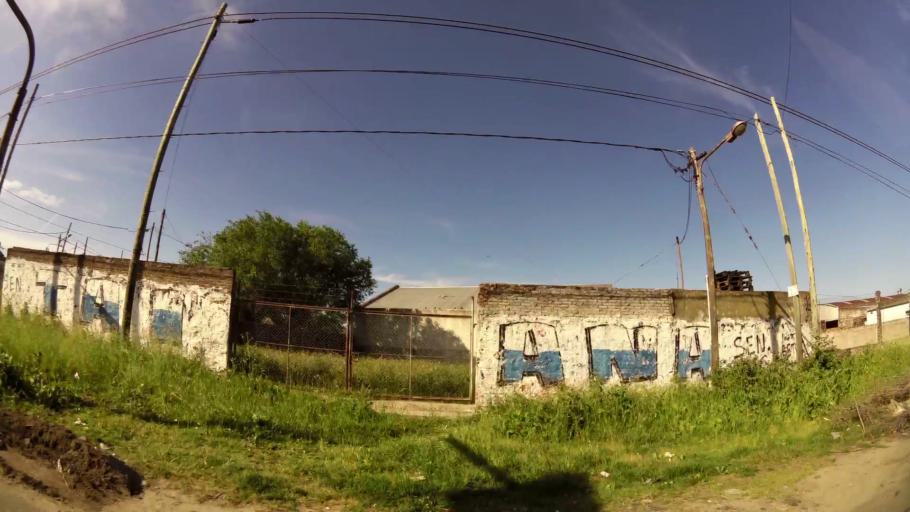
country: AR
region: Buenos Aires
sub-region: Partido de Quilmes
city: Quilmes
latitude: -34.7962
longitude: -58.2342
